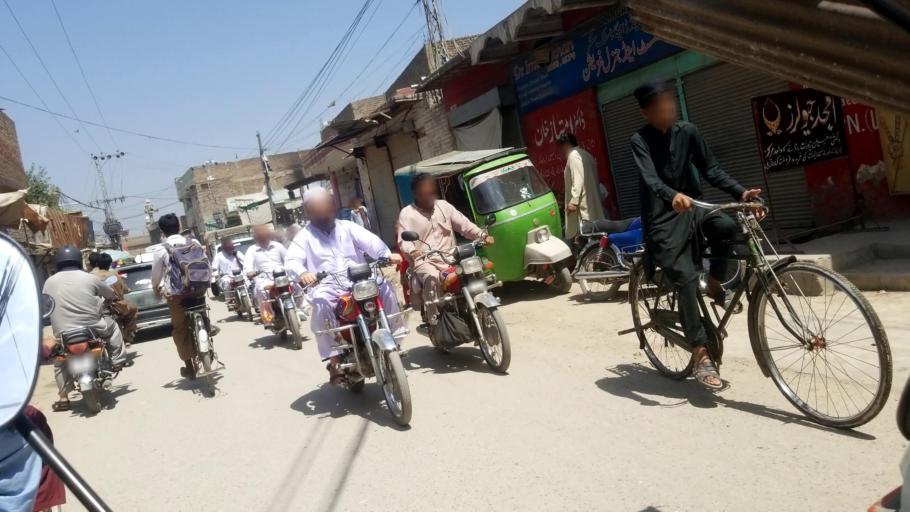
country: PK
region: Khyber Pakhtunkhwa
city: Peshawar
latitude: 34.0272
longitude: 71.4881
